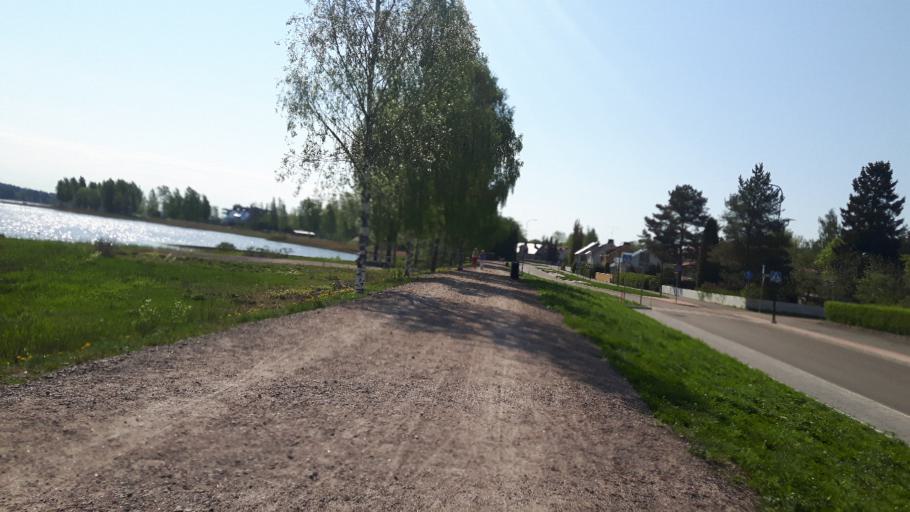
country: FI
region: Uusimaa
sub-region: Loviisa
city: Lovisa
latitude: 60.4501
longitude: 26.2346
